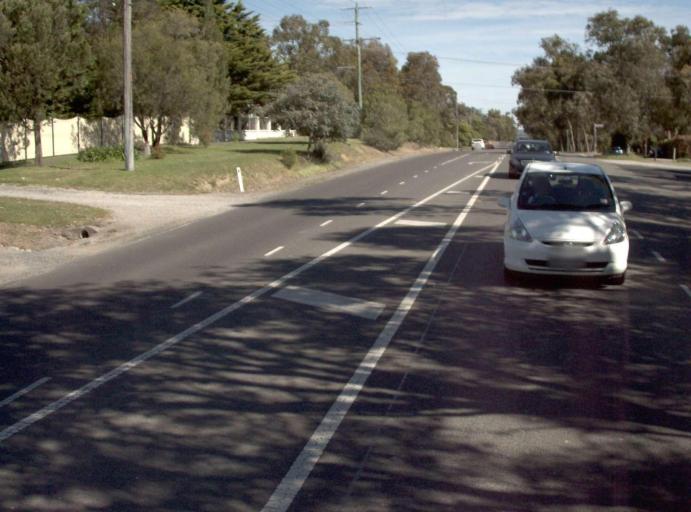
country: AU
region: Victoria
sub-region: Maroondah
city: Croydon South
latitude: -37.8222
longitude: 145.2689
